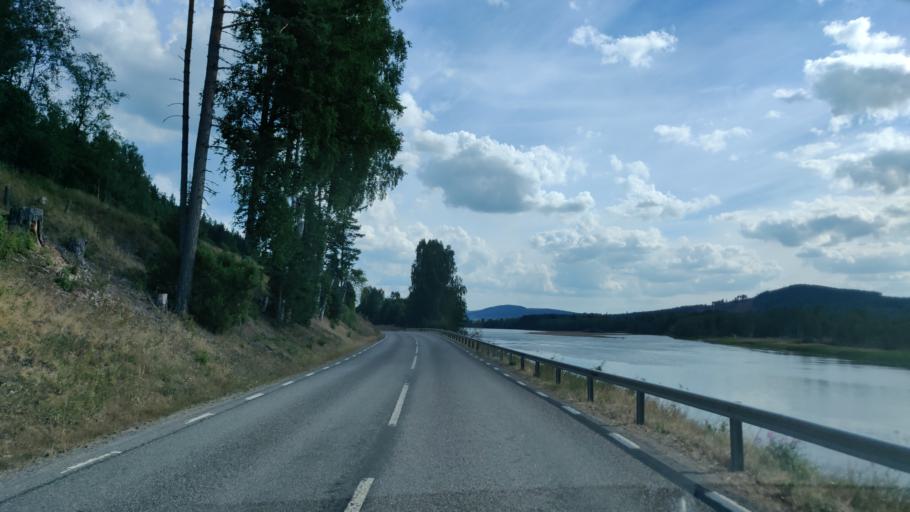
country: SE
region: Vaermland
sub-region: Hagfors Kommun
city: Ekshaerad
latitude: 60.1706
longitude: 13.5295
